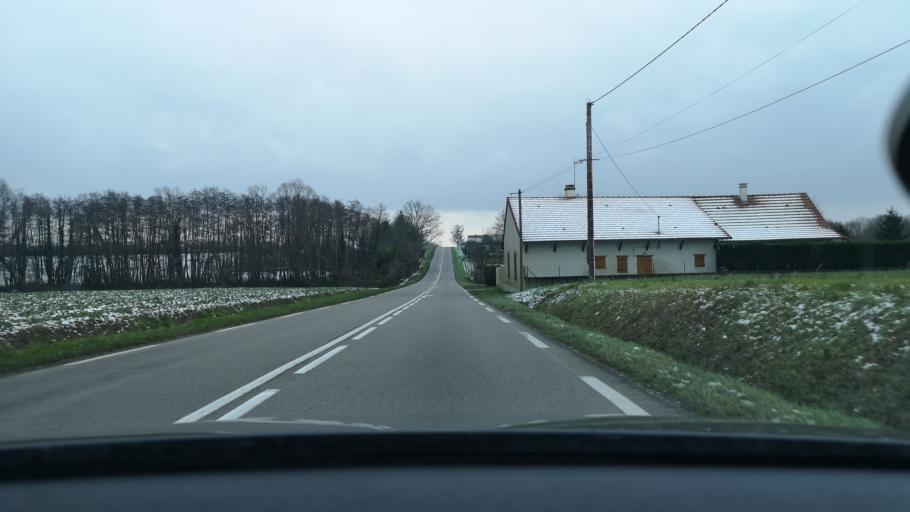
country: FR
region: Bourgogne
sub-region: Departement de Saone-et-Loire
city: Saint-Germain-du-Plain
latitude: 46.7522
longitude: 5.0286
